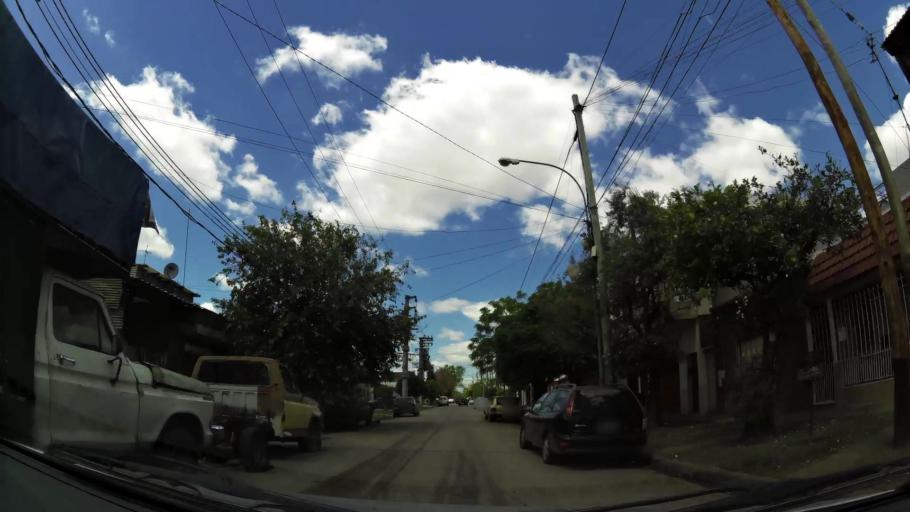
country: AR
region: Buenos Aires
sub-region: Partido de Lanus
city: Lanus
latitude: -34.7109
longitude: -58.4200
